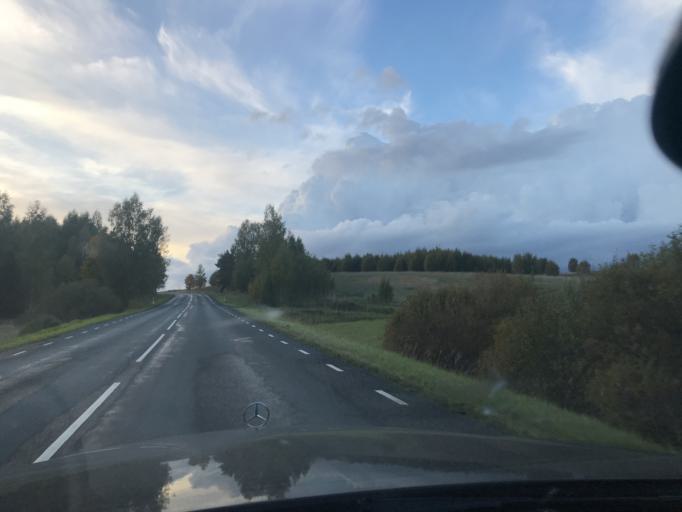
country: EE
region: Vorumaa
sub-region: Antsla vald
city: Vana-Antsla
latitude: 57.9146
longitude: 26.3875
